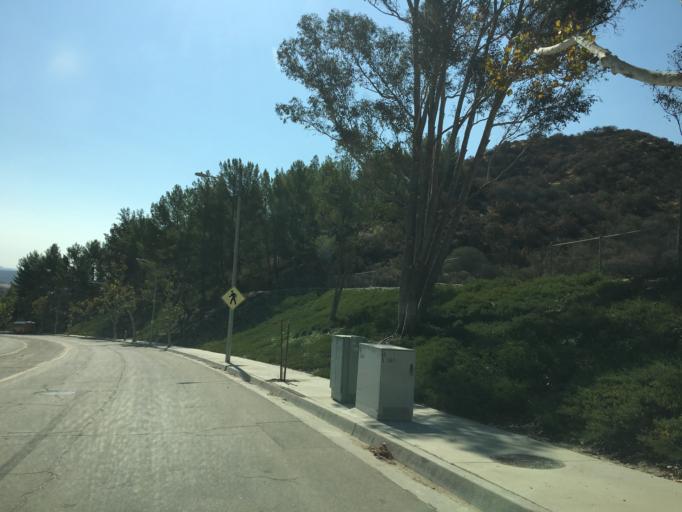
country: US
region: California
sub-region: Los Angeles County
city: Castaic
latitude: 34.4889
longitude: -118.6321
